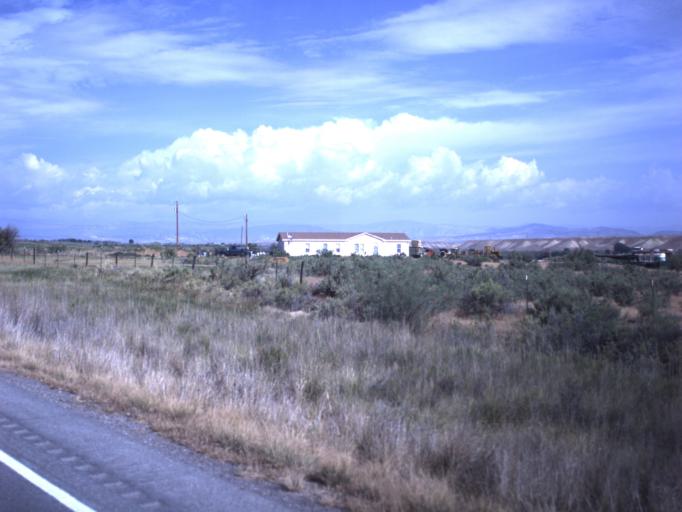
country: US
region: Utah
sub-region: Uintah County
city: Naples
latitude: 40.3786
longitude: -109.4163
